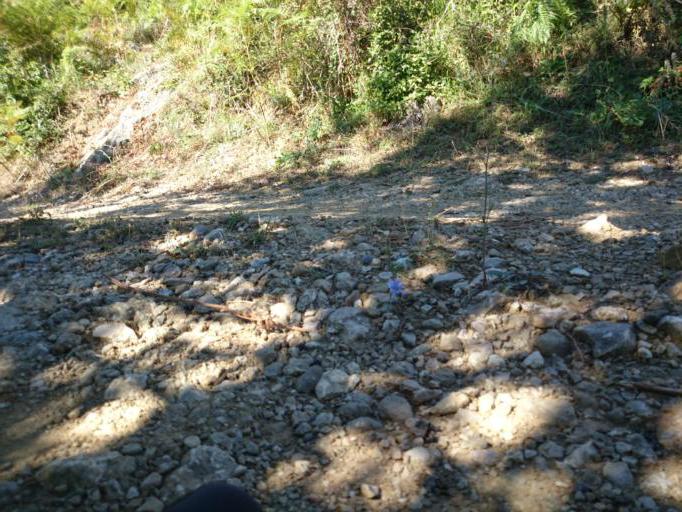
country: AL
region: Elbasan
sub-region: Rrethi i Gramshit
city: Porocan
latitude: 40.9285
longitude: 20.2782
